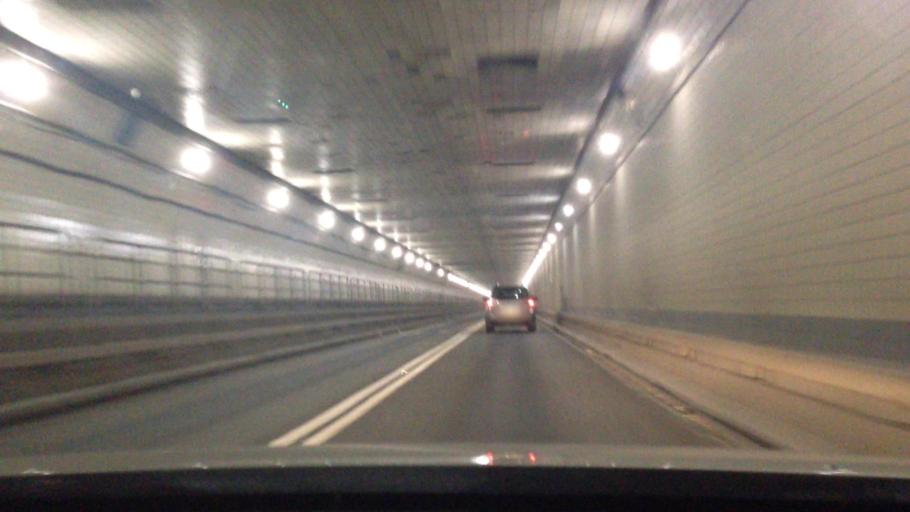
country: US
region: New Jersey
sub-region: Hudson County
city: Weehawken
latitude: 40.7611
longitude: -74.0064
